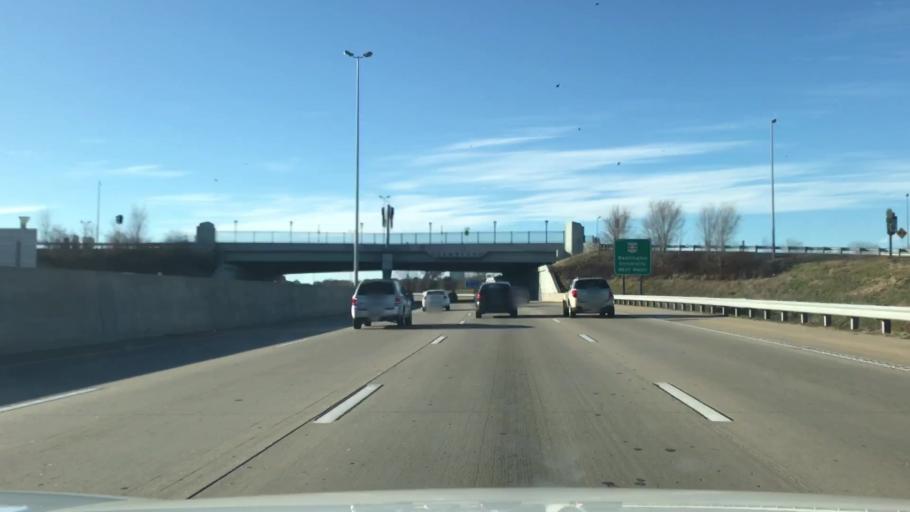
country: US
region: Missouri
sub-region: Saint Louis County
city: University City
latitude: 38.6316
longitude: -90.2849
